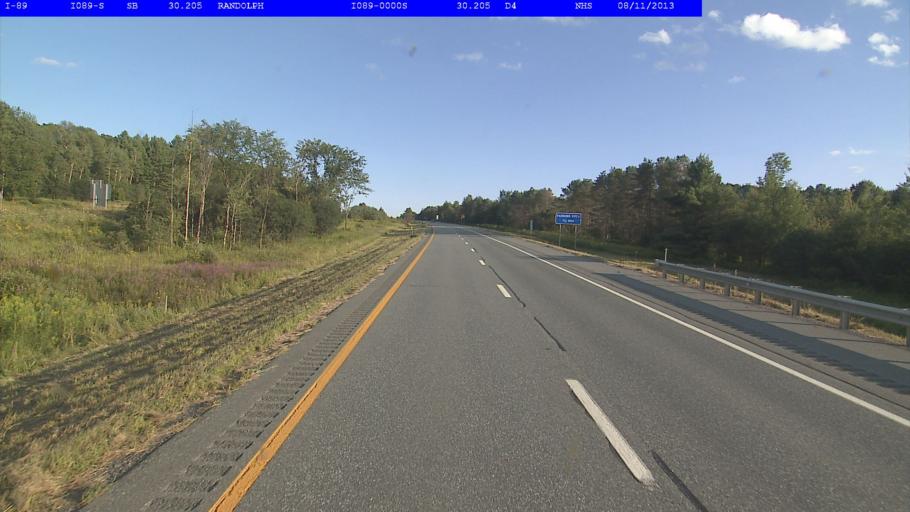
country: US
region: Vermont
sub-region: Orange County
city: Randolph
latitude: 43.9351
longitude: -72.6214
